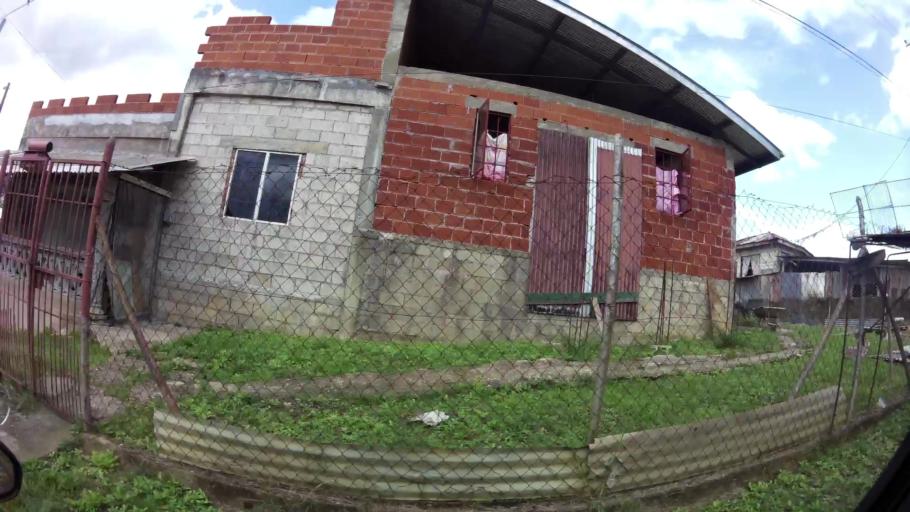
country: TT
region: City of San Fernando
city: Mon Repos
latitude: 10.2737
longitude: -61.4479
